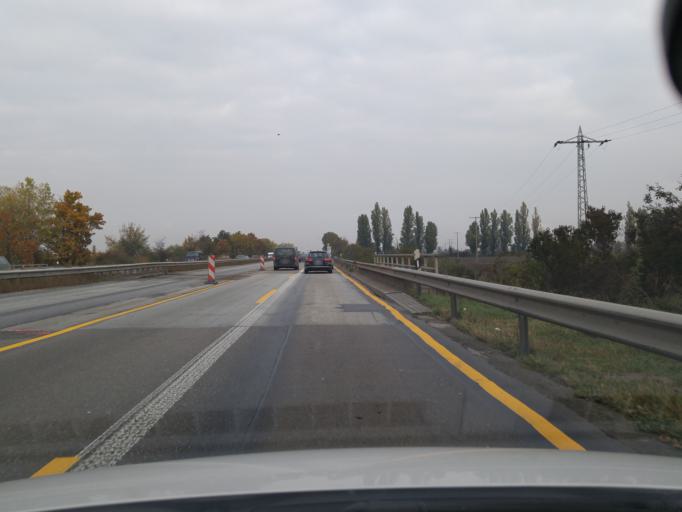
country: DE
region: Rheinland-Pfalz
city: Maxdorf
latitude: 49.4946
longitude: 8.3120
